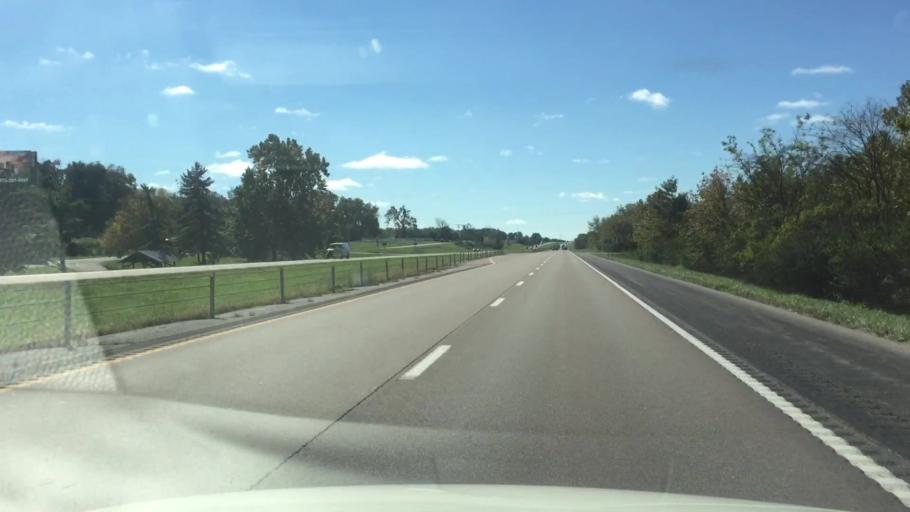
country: US
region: Missouri
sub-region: Boone County
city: Ashland
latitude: 38.8124
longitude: -92.2515
